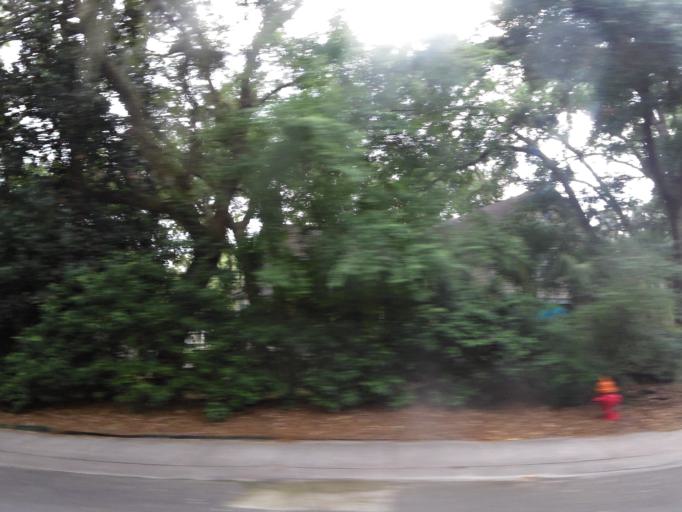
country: US
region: Georgia
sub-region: Glynn County
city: Saint Simons Island
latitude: 31.1566
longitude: -81.3805
